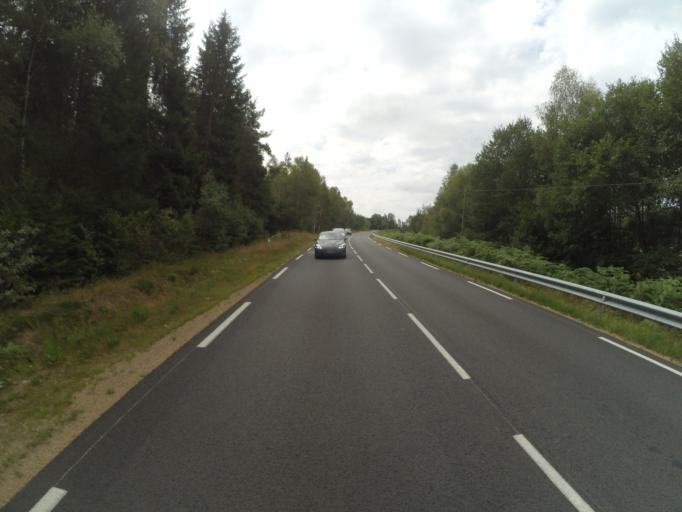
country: FR
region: Limousin
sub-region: Departement de la Creuse
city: La Courtine
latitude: 45.6307
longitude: 2.2768
